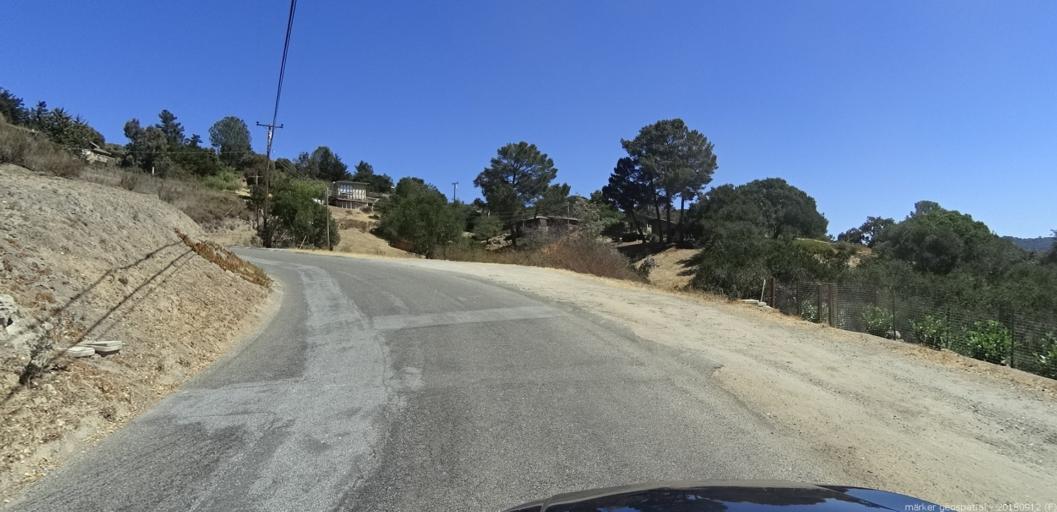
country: US
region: California
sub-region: Monterey County
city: Carmel Valley Village
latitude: 36.4880
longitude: -121.7360
